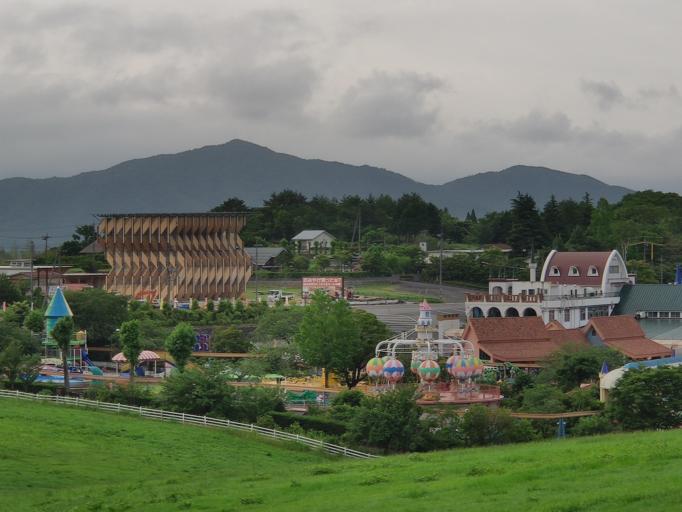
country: JP
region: Tottori
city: Kurayoshi
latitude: 35.2936
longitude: 133.6320
